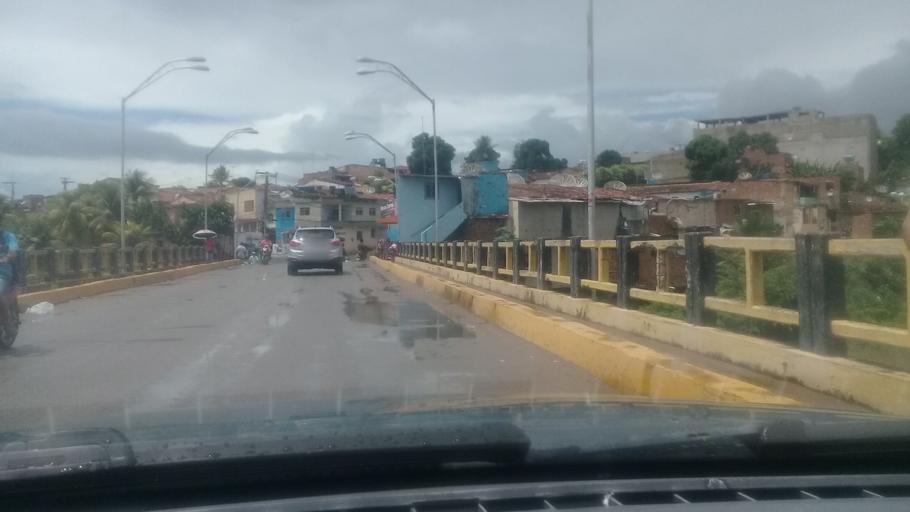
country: BR
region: Pernambuco
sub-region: Vitoria De Santo Antao
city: Vitoria de Santo Antao
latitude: -8.1229
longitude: -35.2942
